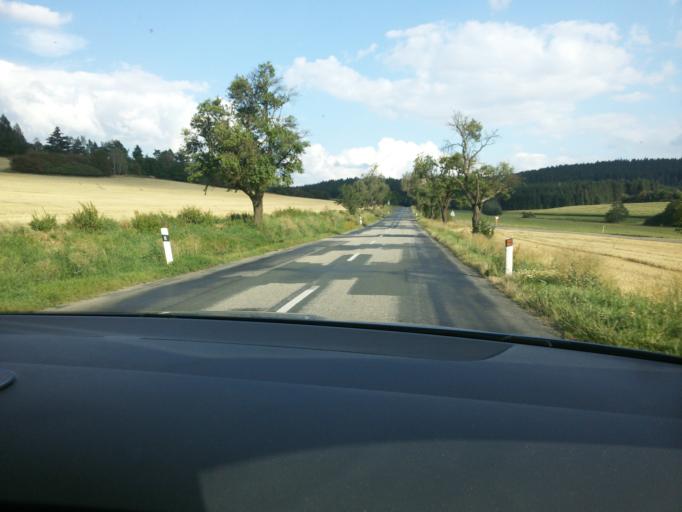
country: CZ
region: South Moravian
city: Olesnice
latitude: 49.5395
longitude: 16.4427
